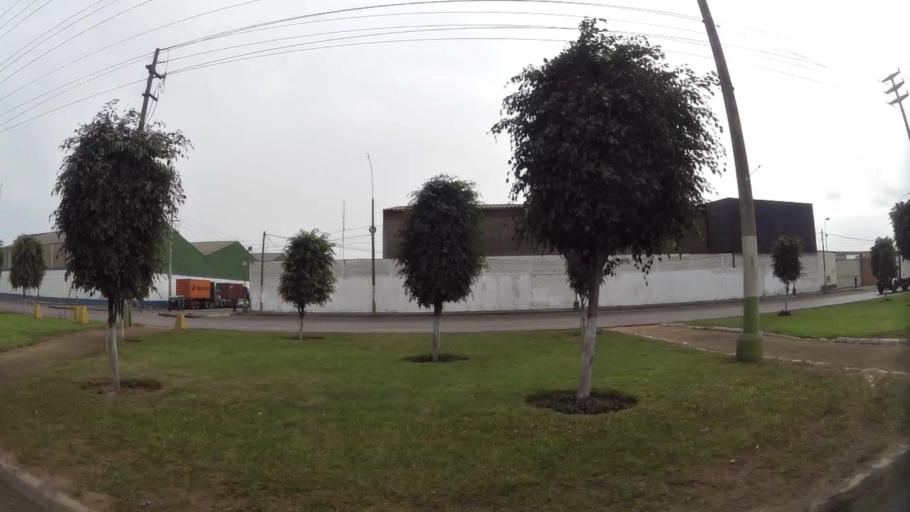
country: PE
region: Callao
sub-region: Callao
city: Callao
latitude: -12.0161
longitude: -77.1030
